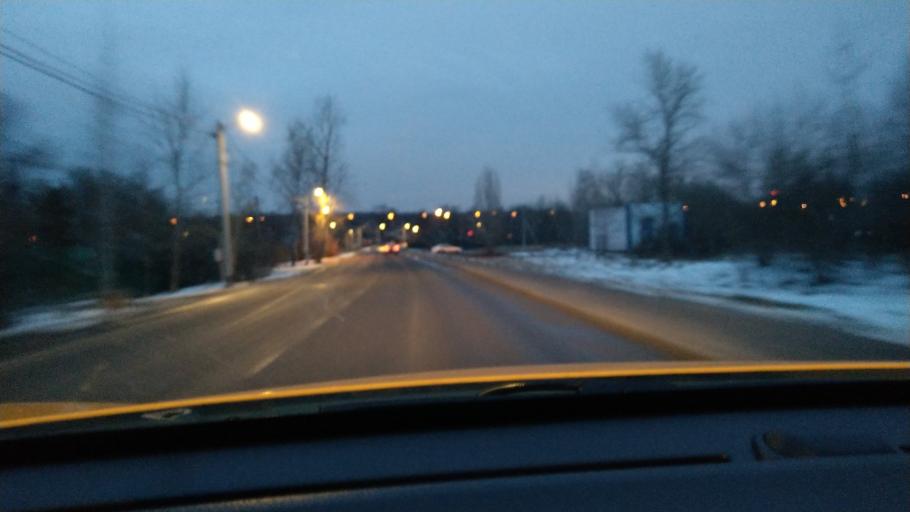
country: RU
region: Moskovskaya
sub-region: Leninskiy Rayon
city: Vnukovo
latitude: 55.6173
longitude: 37.2698
